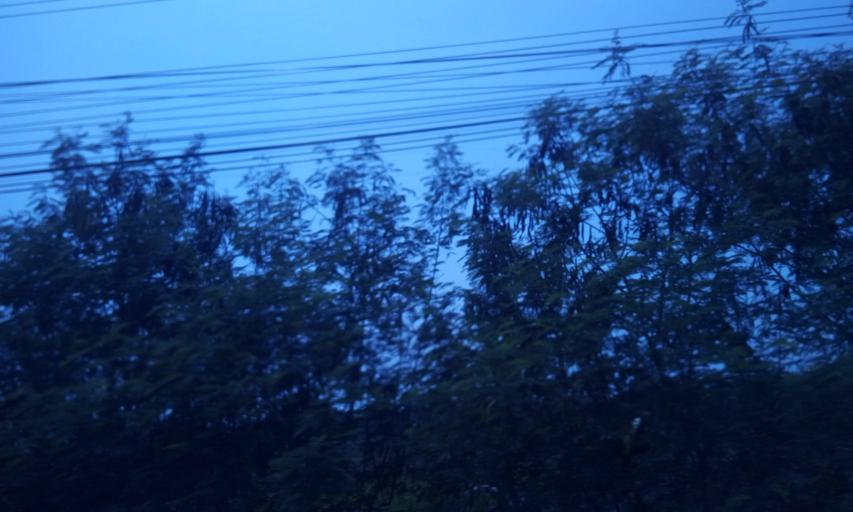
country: TH
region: Nonthaburi
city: Sai Noi
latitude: 13.9590
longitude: 100.3110
